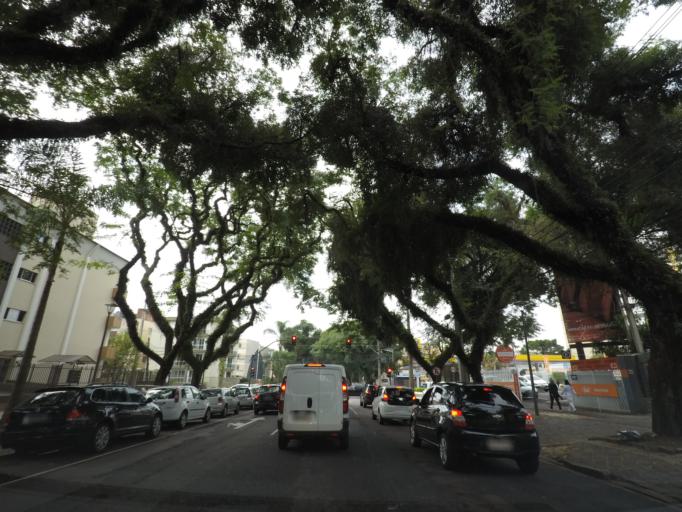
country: BR
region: Parana
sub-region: Curitiba
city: Curitiba
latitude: -25.4492
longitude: -49.2829
